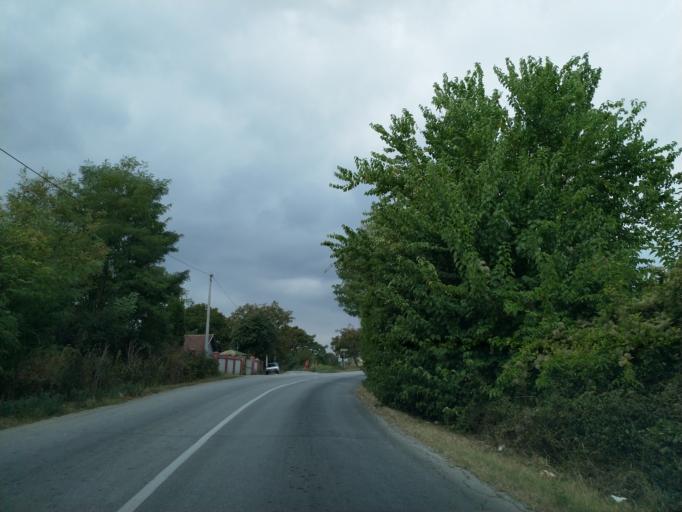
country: RS
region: Central Serbia
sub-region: Pomoravski Okrug
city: Jagodina
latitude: 43.9918
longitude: 21.2279
